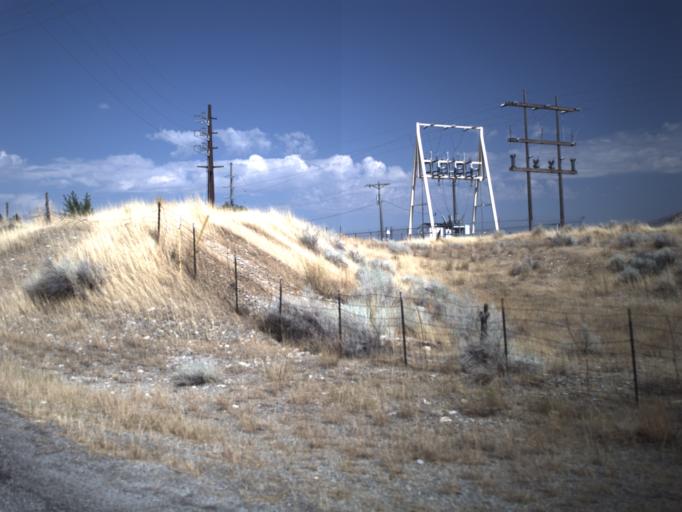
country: US
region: Utah
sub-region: Cache County
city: Hyrum
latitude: 41.6332
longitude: -111.8133
